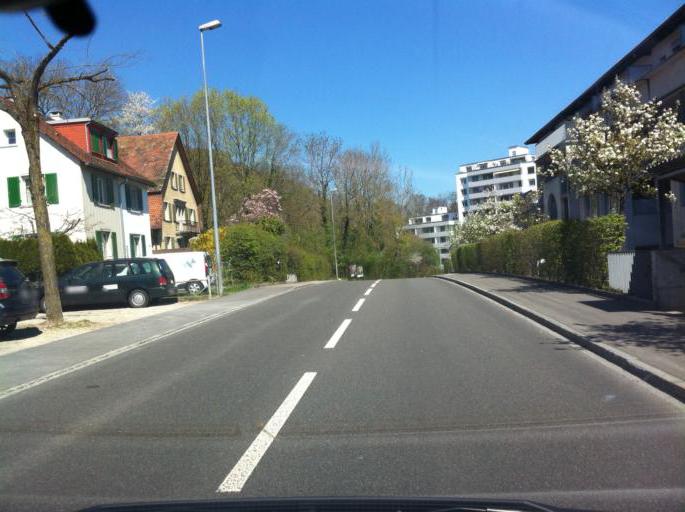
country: CH
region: Schaffhausen
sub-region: Bezirk Schaffhausen
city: Schaffhausen
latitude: 47.7110
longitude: 8.6296
